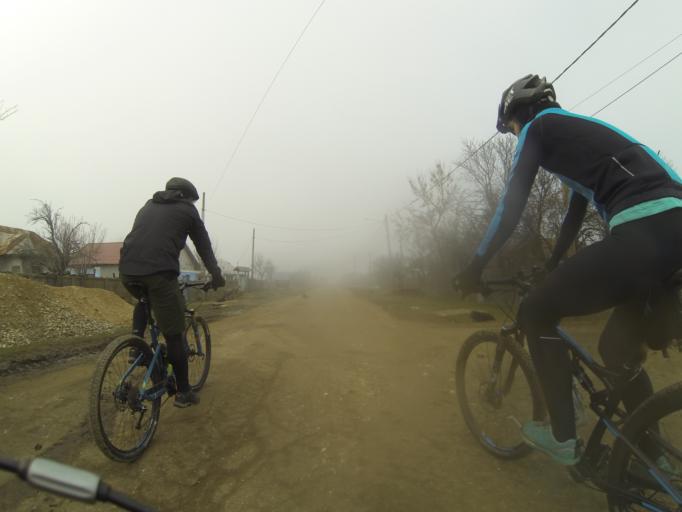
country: RO
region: Mehedinti
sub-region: Comuna Baclesu
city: Baclesu
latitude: 44.4792
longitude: 23.1086
